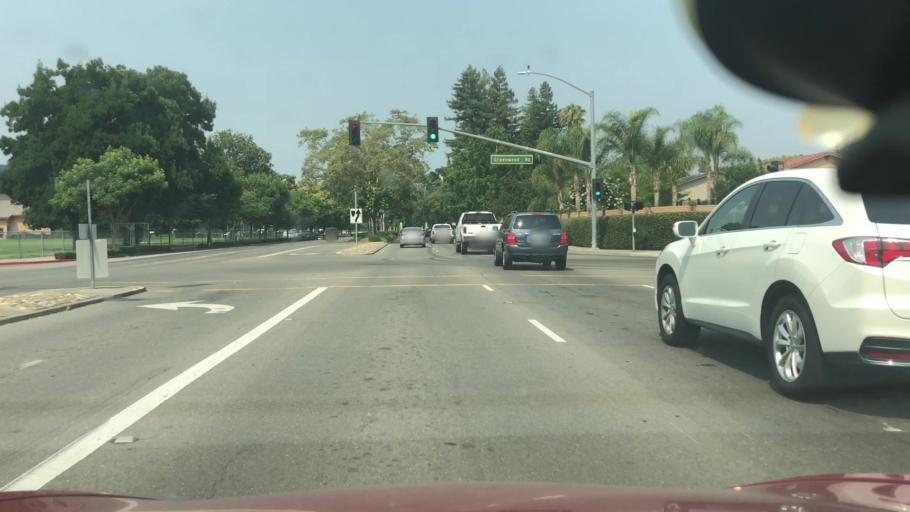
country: US
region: California
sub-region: Alameda County
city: Pleasanton
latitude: 37.6767
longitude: -121.8802
